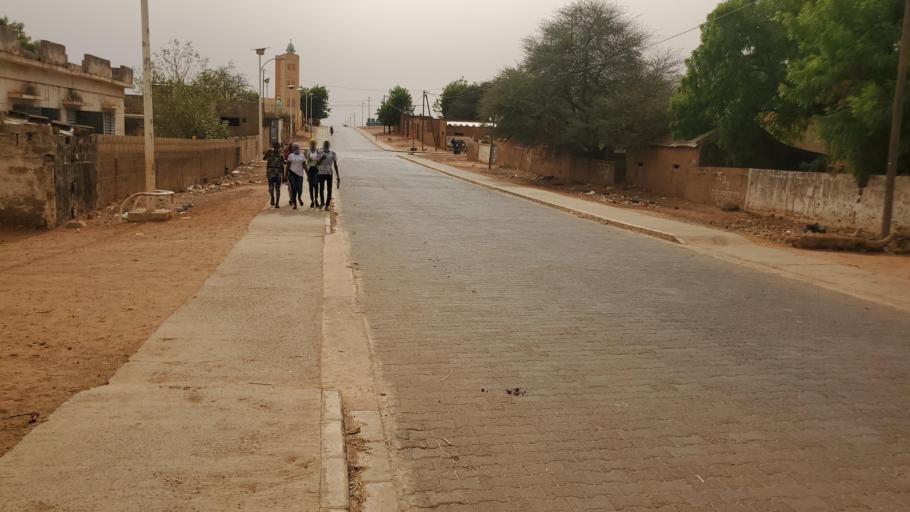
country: SN
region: Louga
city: Ndibene Dahra
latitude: 15.4006
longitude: -15.1183
